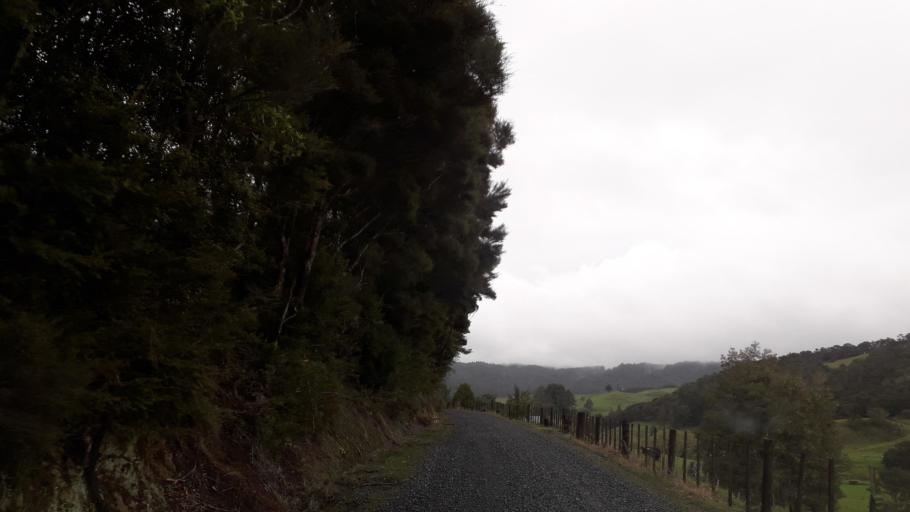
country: NZ
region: Northland
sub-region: Far North District
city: Waimate North
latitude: -35.1447
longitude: 173.7129
